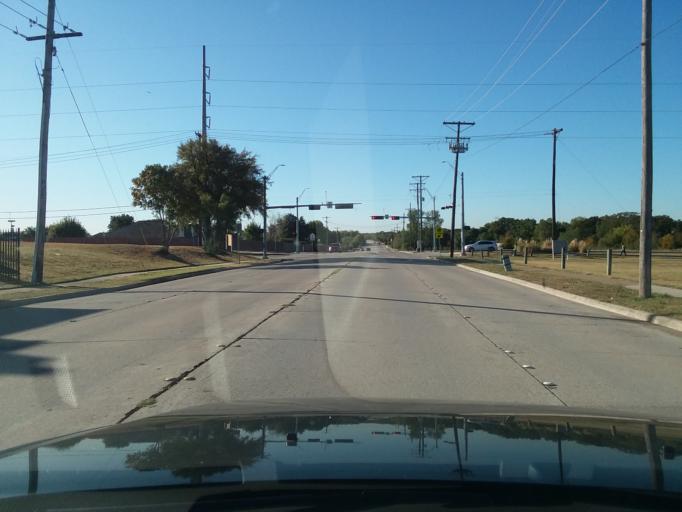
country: US
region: Texas
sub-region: Denton County
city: Lewisville
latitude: 33.0284
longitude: -97.0277
